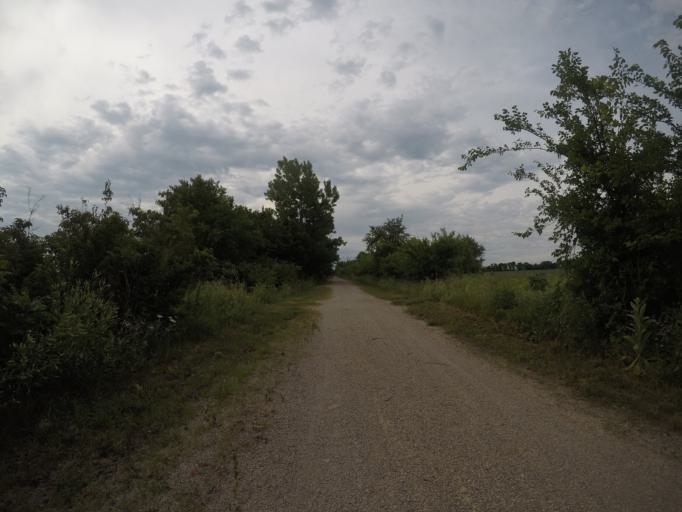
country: US
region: Kansas
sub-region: Franklin County
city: Ottawa
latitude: 38.4554
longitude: -95.2685
